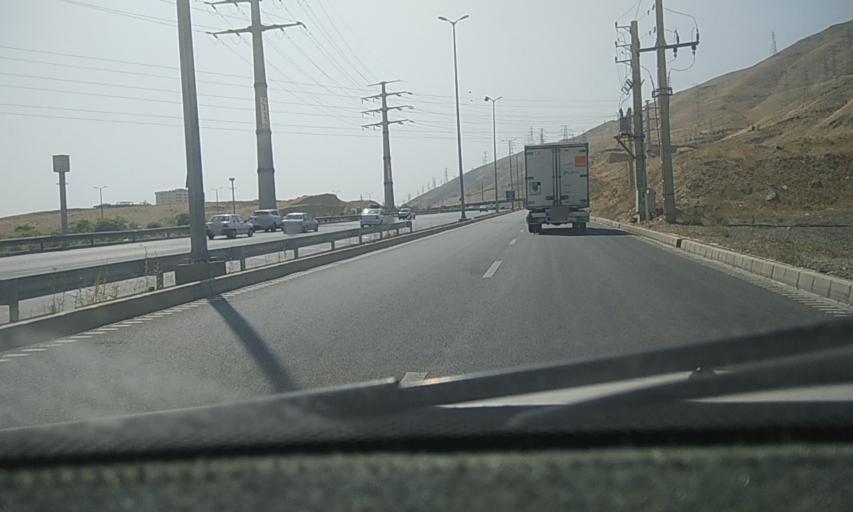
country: IR
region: Tehran
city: Shahr-e Qods
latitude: 35.7617
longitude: 51.1652
